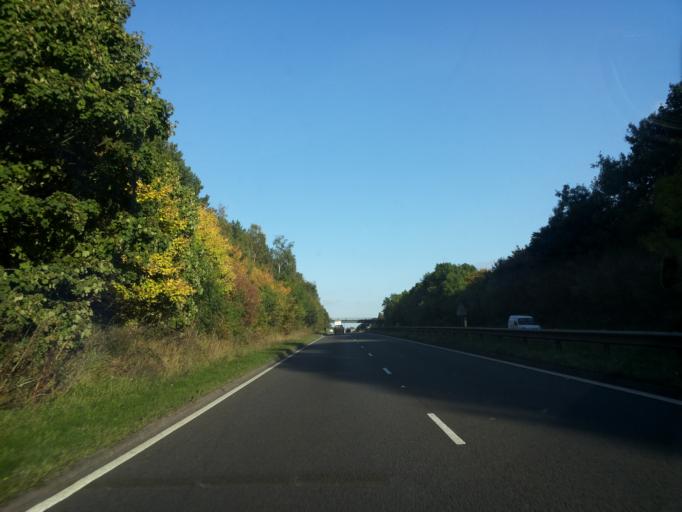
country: GB
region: England
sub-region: Derbyshire
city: Pilsley
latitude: 53.2008
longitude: -1.3495
